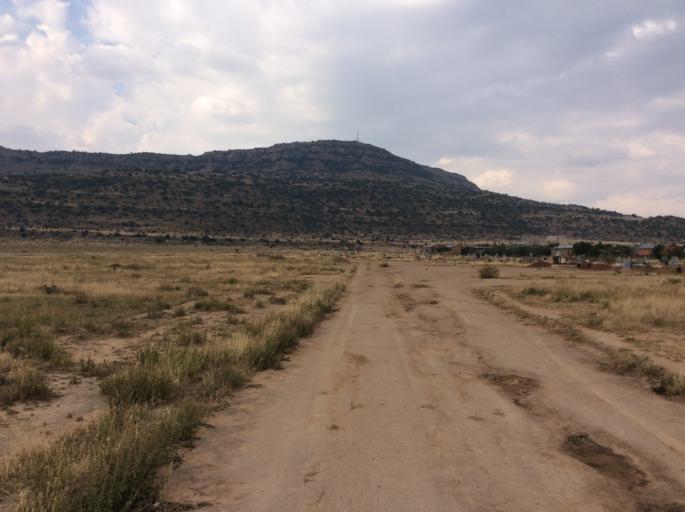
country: LS
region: Mafeteng
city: Mafeteng
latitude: -29.7086
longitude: 27.0123
